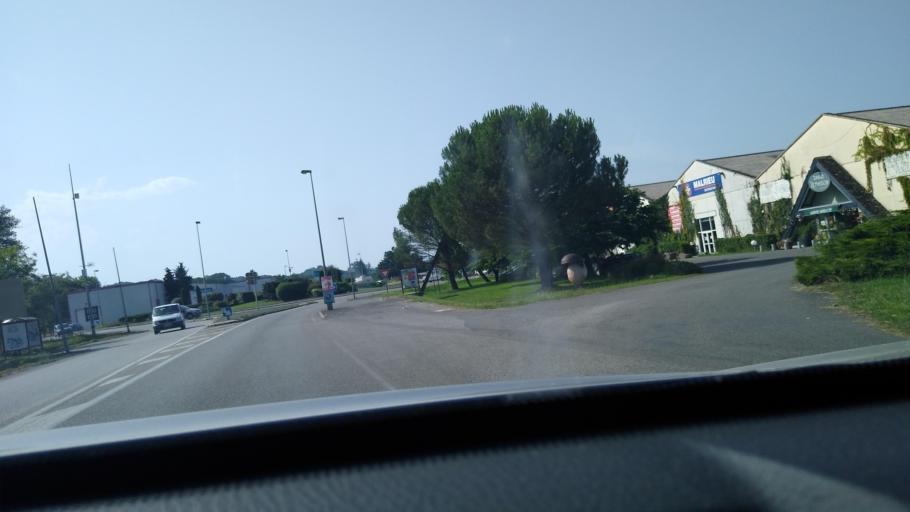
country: FR
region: Midi-Pyrenees
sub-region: Departement de l'Ariege
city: Saint-Lizier
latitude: 43.0201
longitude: 1.1005
